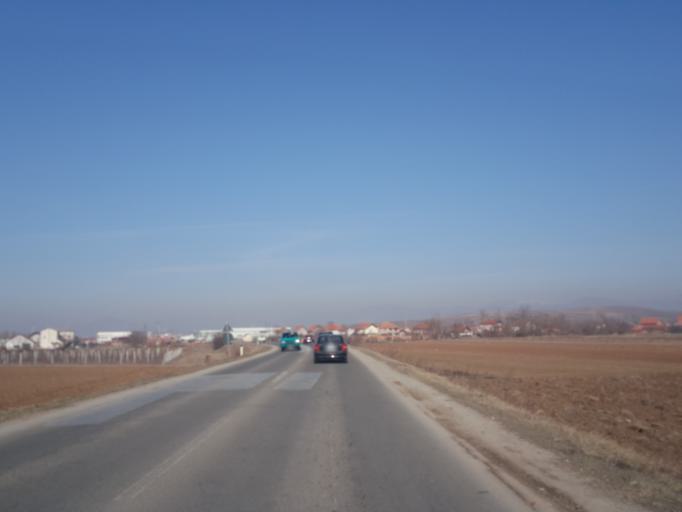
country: XK
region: Mitrovica
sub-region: Vushtrri
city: Vushtrri
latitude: 42.7793
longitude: 21.0139
